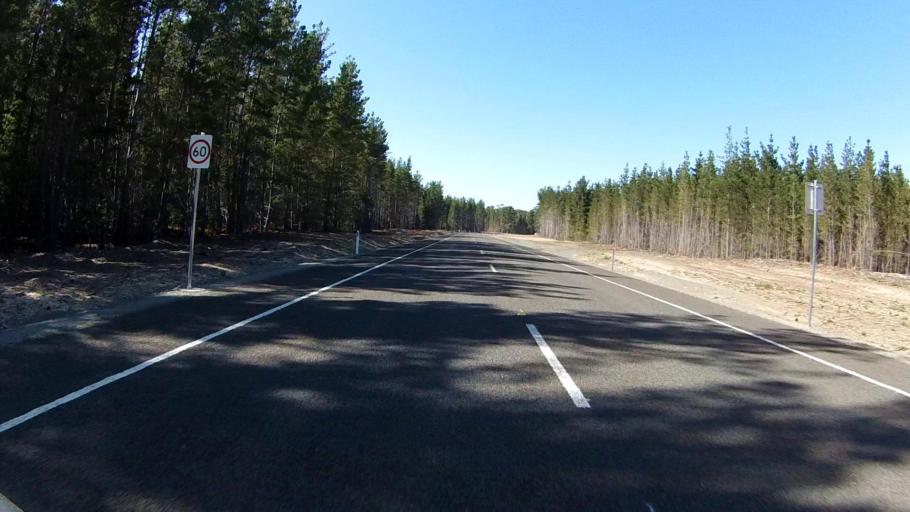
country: AU
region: Tasmania
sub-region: Clarence
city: Seven Mile Beach
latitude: -42.8472
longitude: 147.5157
